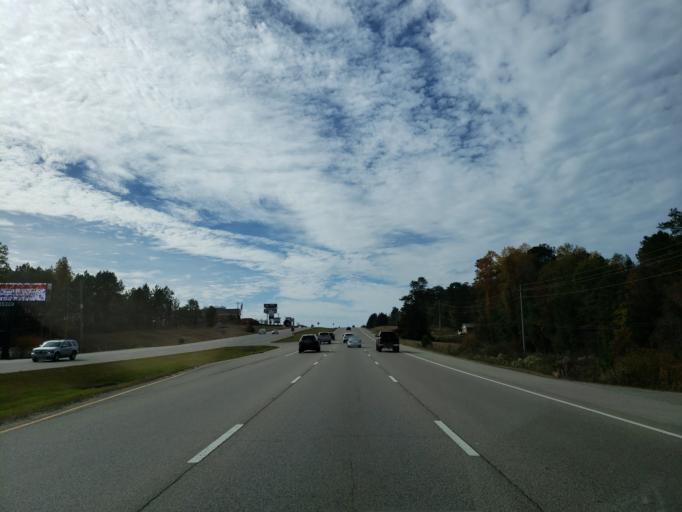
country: US
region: Mississippi
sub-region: Lamar County
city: West Hattiesburg
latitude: 31.3205
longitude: -89.3893
